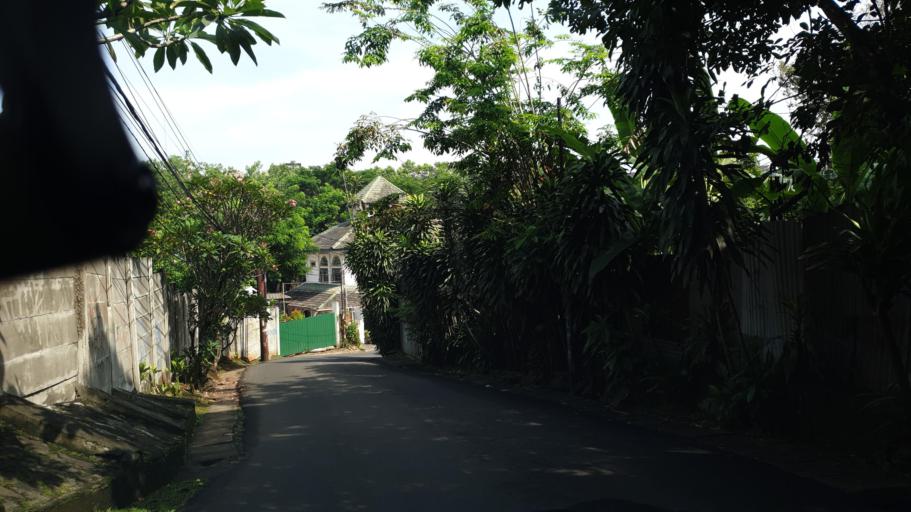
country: ID
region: Banten
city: South Tangerang
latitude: -6.3014
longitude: 106.7643
